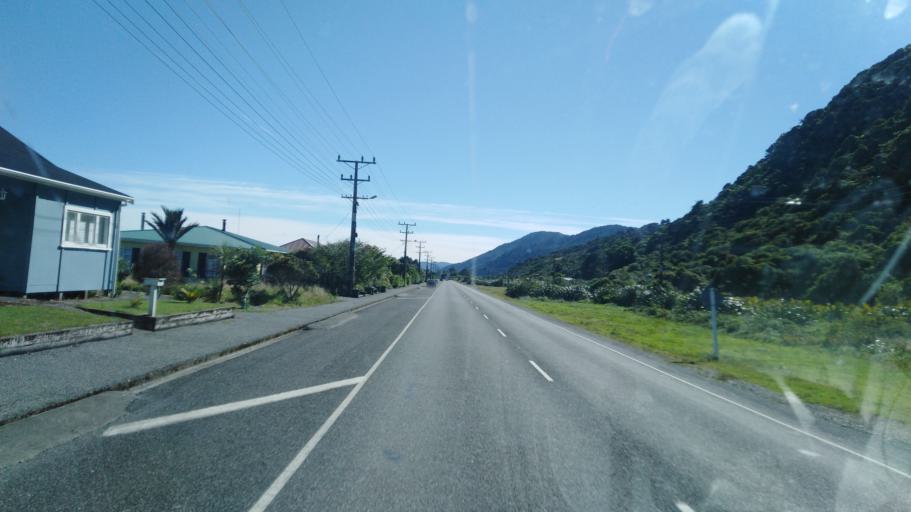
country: NZ
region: West Coast
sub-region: Buller District
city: Westport
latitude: -41.6237
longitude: 171.8595
